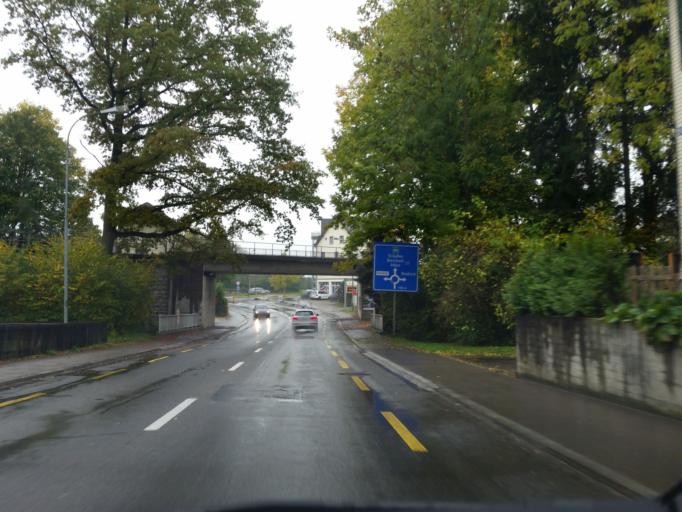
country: CH
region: Thurgau
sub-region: Arbon District
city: Egnach
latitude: 47.5420
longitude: 9.3773
